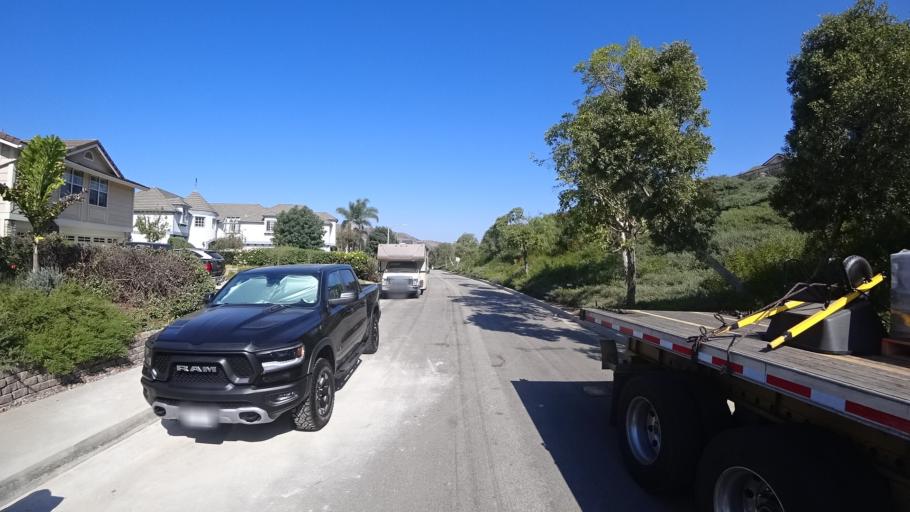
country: US
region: California
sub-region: Orange County
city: San Clemente
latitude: 33.4626
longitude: -117.6346
